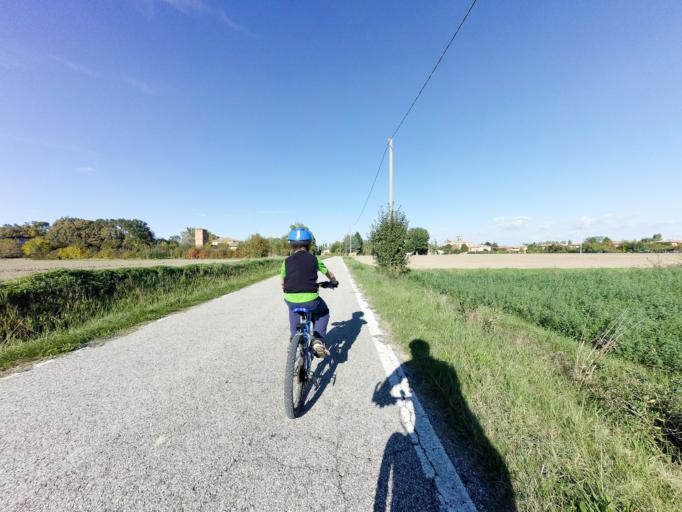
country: IT
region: Emilia-Romagna
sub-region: Provincia di Bologna
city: Bentivoglio
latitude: 44.6012
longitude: 11.4171
